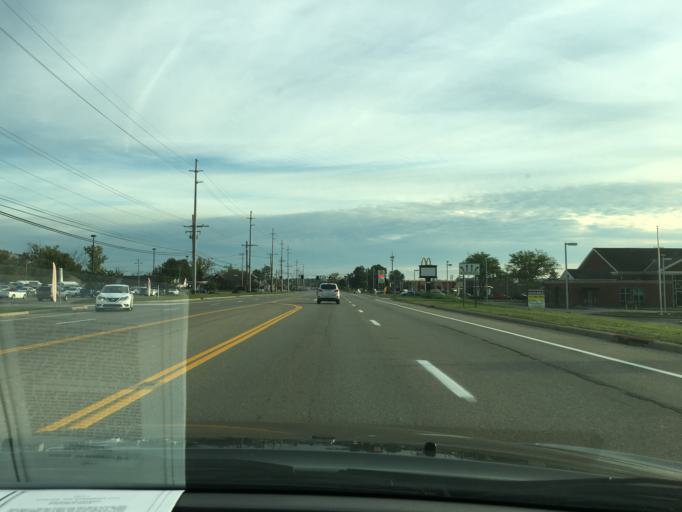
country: US
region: Ohio
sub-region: Butler County
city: Beckett Ridge
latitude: 39.3537
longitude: -84.4613
